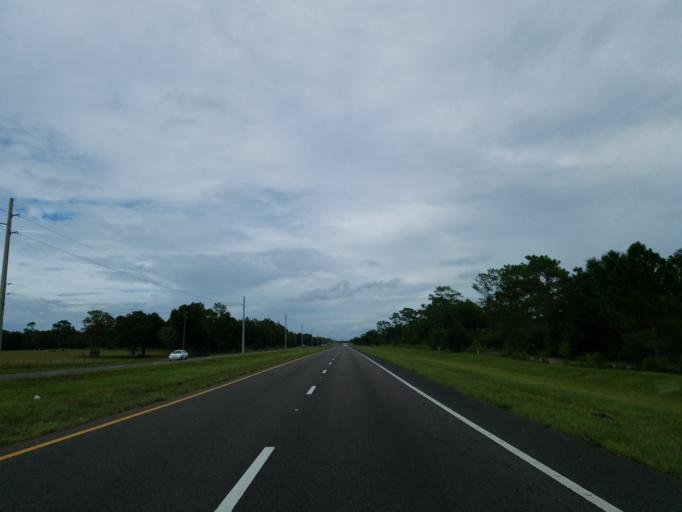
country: US
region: Florida
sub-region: Sumter County
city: Wildwood
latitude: 28.8662
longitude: -82.1500
